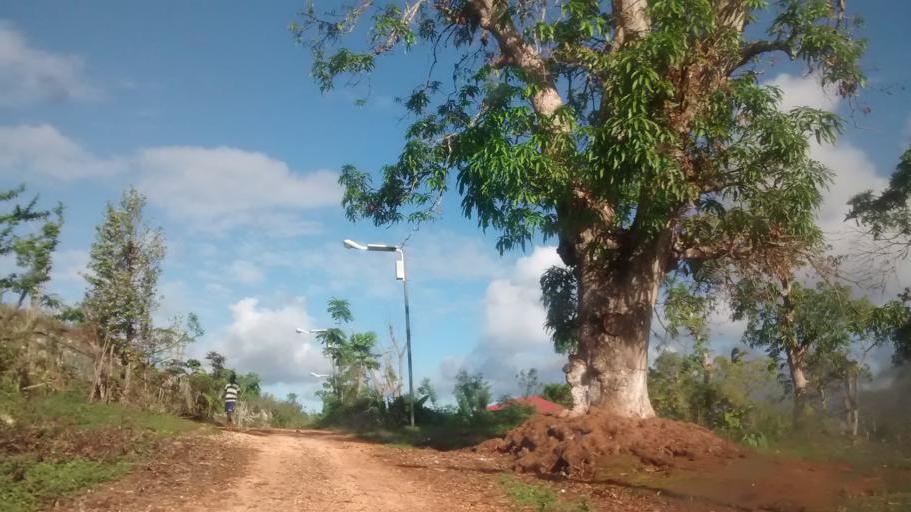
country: HT
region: Grandans
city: Corail
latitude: 18.5311
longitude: -73.8477
